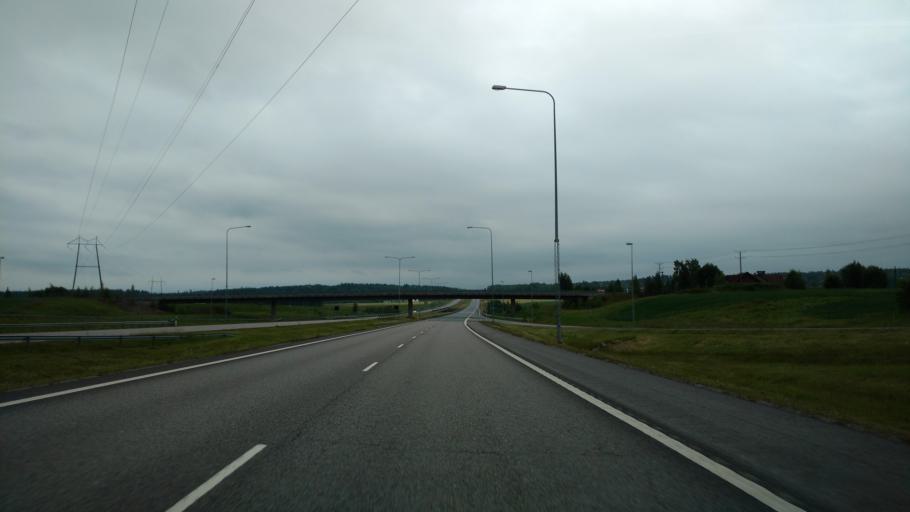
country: FI
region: Varsinais-Suomi
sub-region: Salo
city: Salo
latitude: 60.4169
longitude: 23.1687
